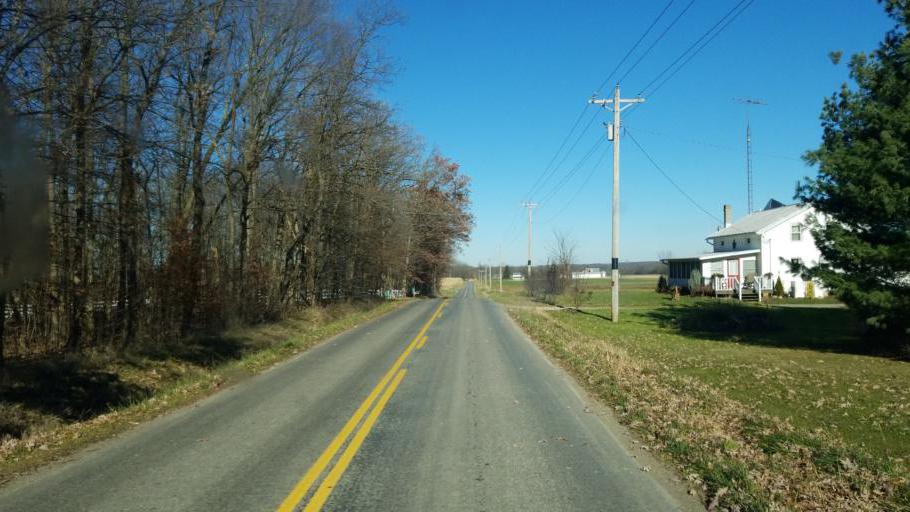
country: US
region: Ohio
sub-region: Ashland County
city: Ashland
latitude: 40.9178
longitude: -82.3876
